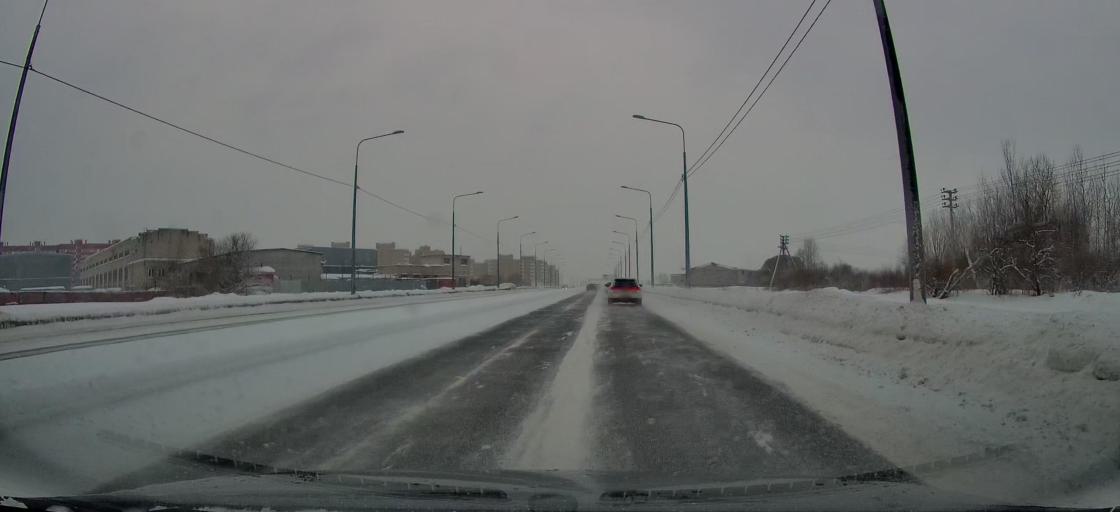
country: RU
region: St.-Petersburg
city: Krasnoye Selo
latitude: 59.7503
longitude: 30.0860
